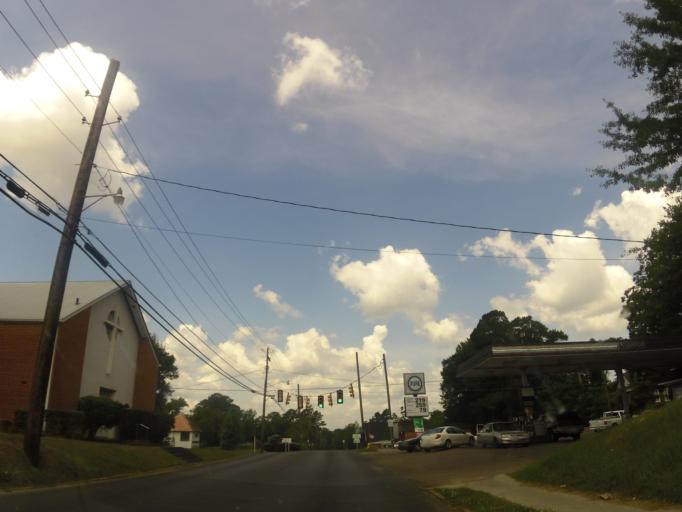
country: US
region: Mississippi
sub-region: Lauderdale County
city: Meridian
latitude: 32.3780
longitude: -88.7125
